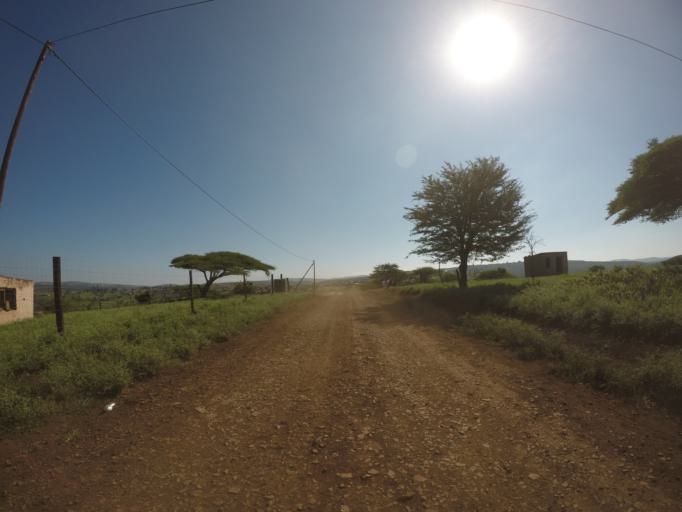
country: ZA
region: KwaZulu-Natal
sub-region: uThungulu District Municipality
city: Empangeni
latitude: -28.5712
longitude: 31.7328
